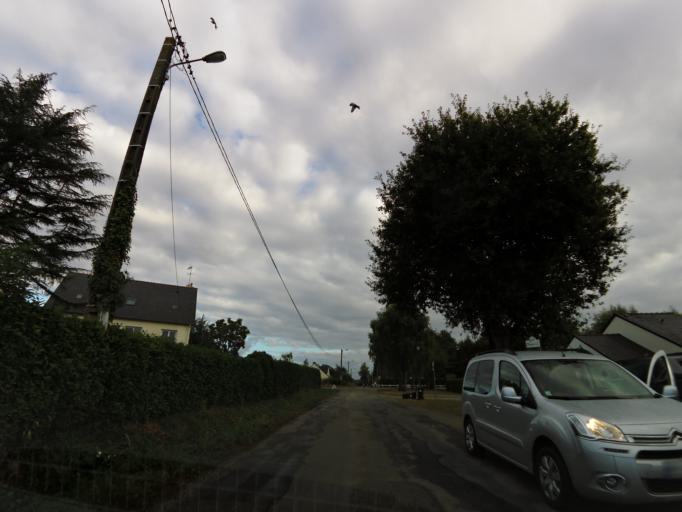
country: FR
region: Brittany
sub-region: Departement d'Ille-et-Vilaine
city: Crevin
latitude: 47.9378
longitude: -1.6543
